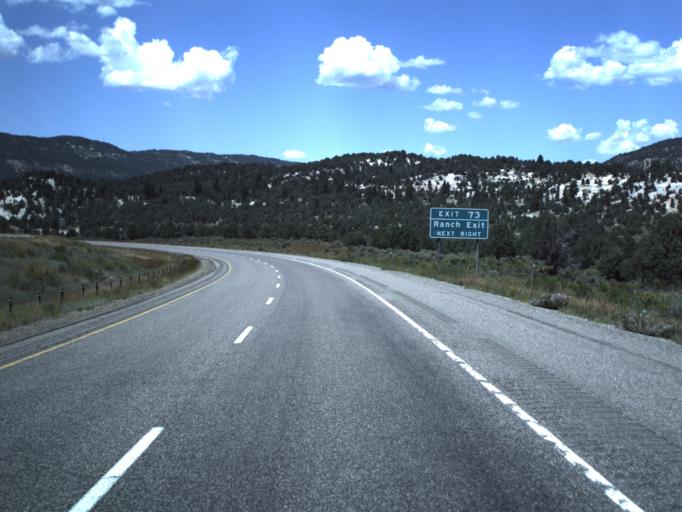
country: US
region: Utah
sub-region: Sevier County
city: Salina
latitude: 38.8740
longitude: -111.5538
